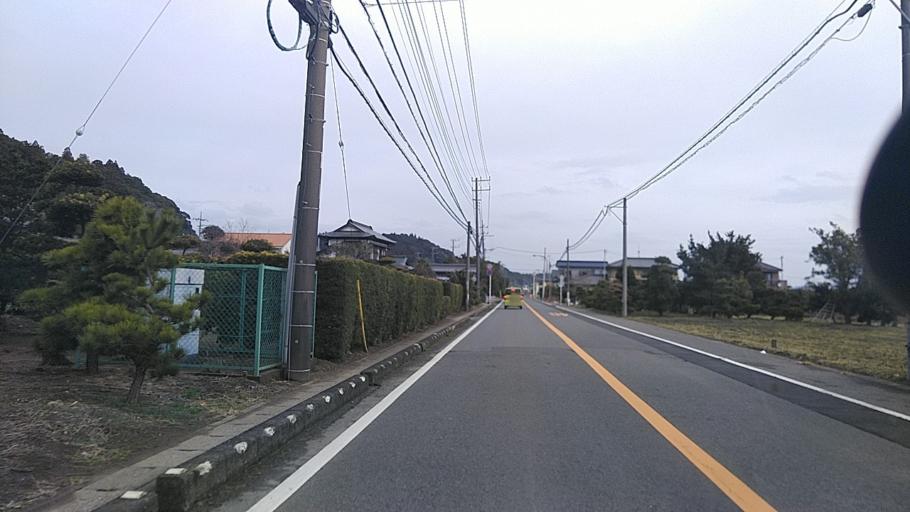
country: JP
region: Chiba
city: Naruto
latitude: 35.5863
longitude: 140.3828
